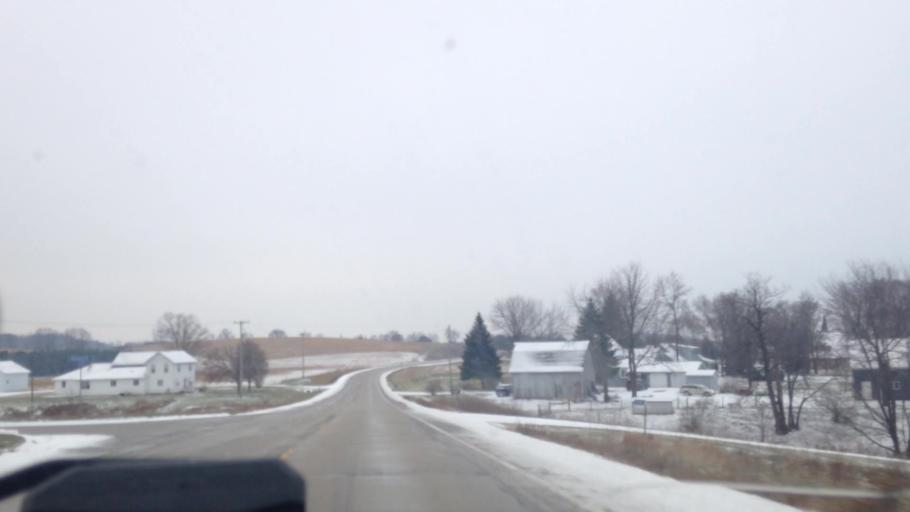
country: US
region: Wisconsin
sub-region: Jefferson County
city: Ixonia
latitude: 43.2395
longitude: -88.5183
